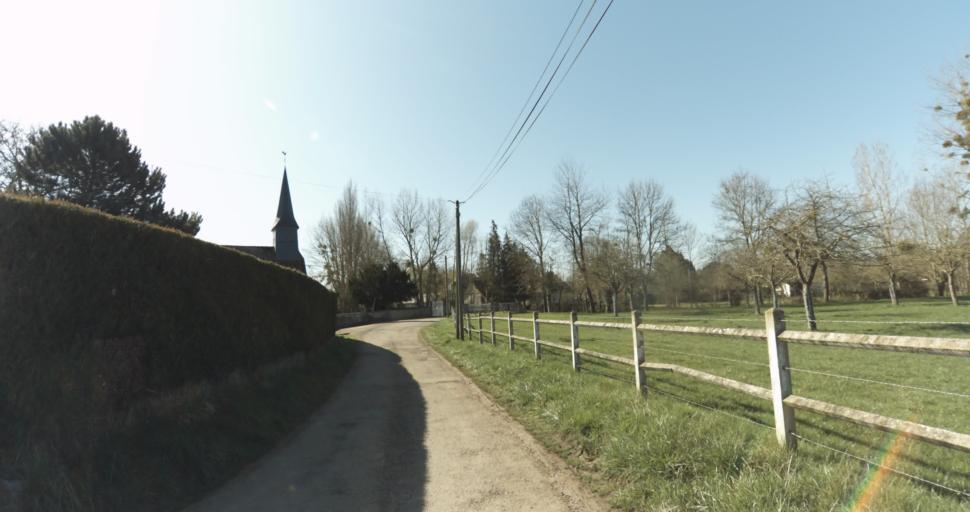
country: FR
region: Lower Normandy
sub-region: Departement du Calvados
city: Saint-Pierre-sur-Dives
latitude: 48.9767
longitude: 0.0399
